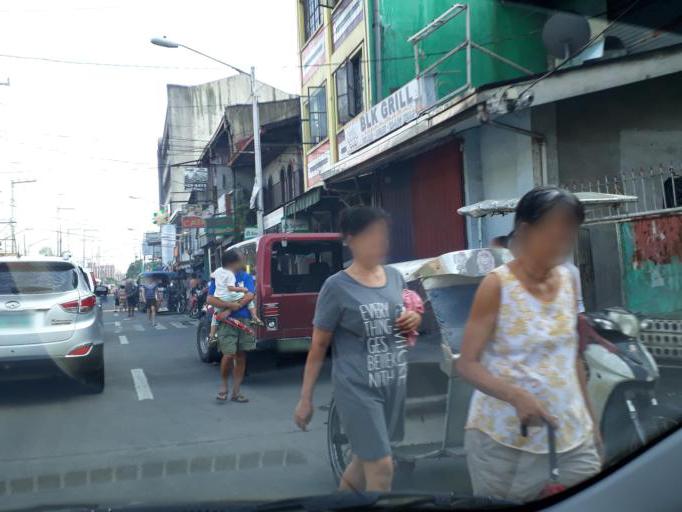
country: PH
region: Metro Manila
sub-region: City of Manila
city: Manila
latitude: 14.6363
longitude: 120.9753
